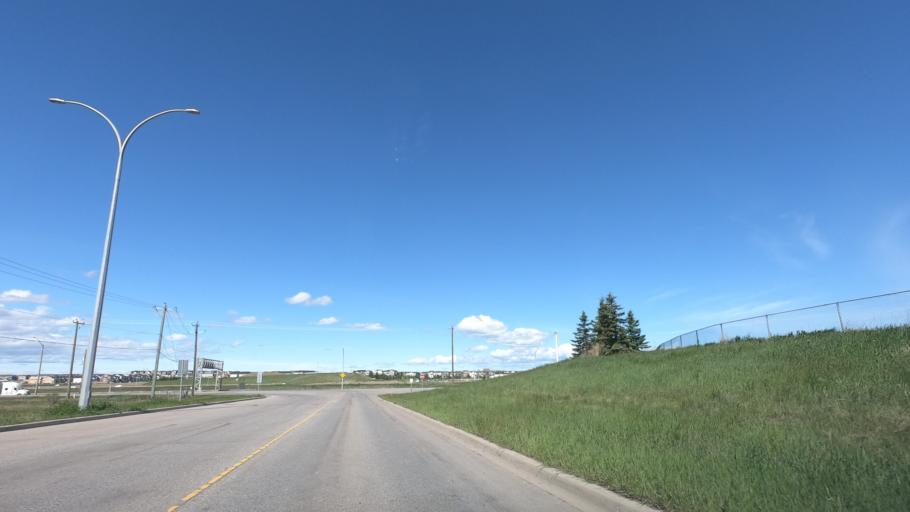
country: CA
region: Alberta
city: Airdrie
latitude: 51.2565
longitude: -113.9991
